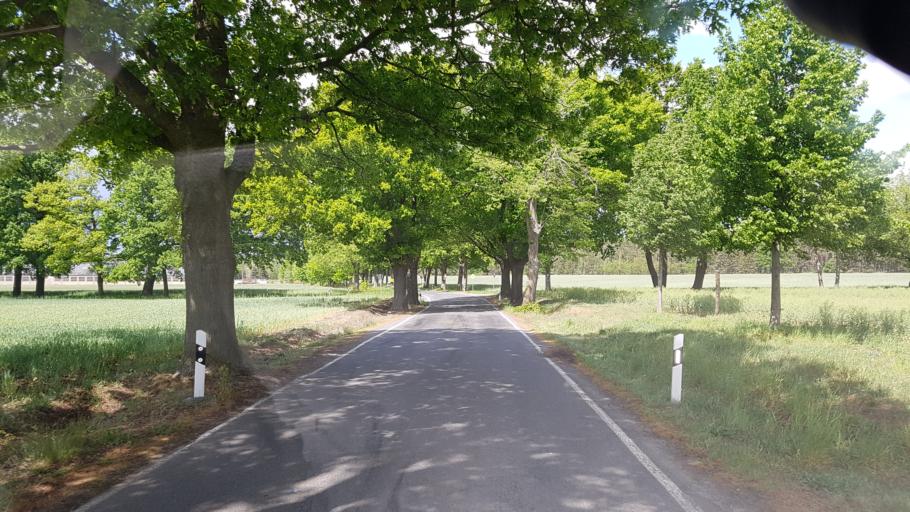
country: DE
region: Brandenburg
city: Bronkow
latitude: 51.6554
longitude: 13.9216
